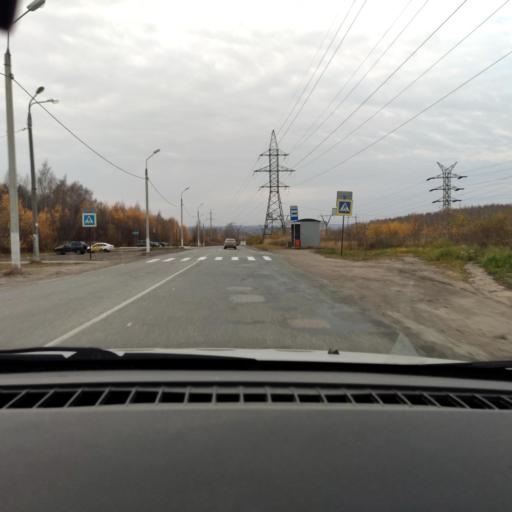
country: RU
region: Perm
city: Perm
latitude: 58.0962
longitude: 56.3992
